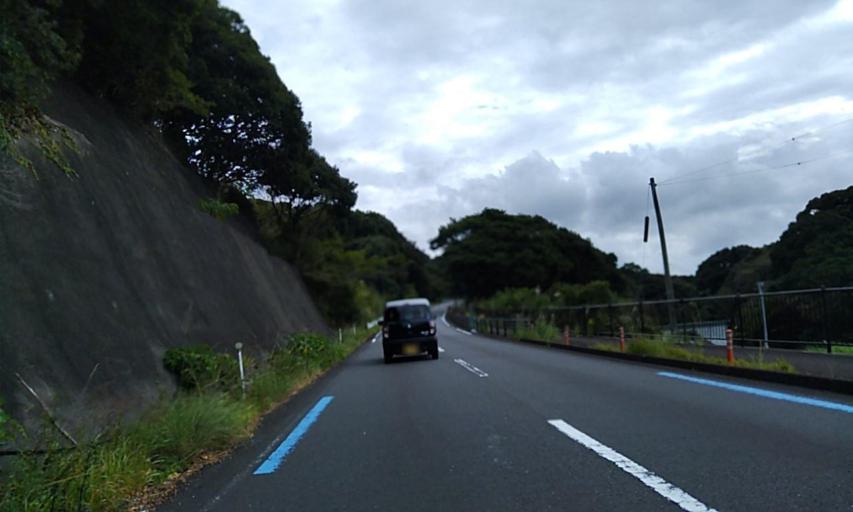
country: JP
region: Wakayama
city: Shingu
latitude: 33.4683
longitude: 135.8256
